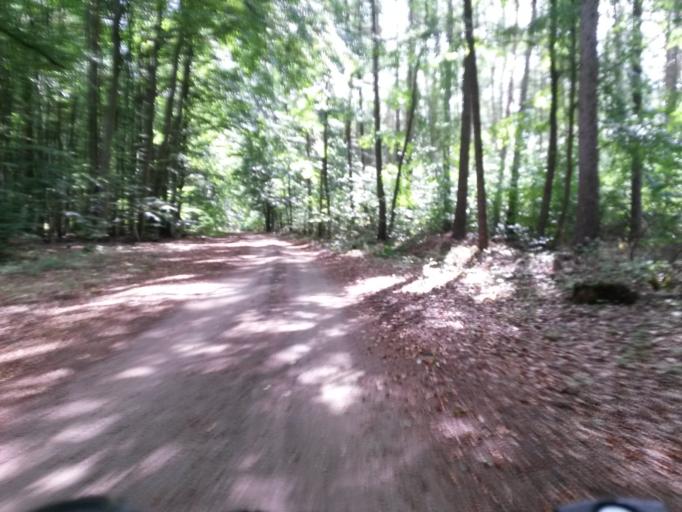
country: DE
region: Brandenburg
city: Templin
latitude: 53.0891
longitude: 13.5368
